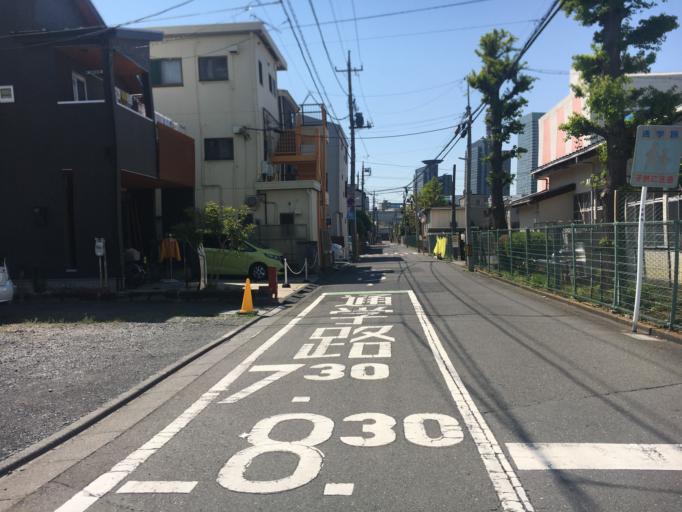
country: JP
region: Saitama
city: Yono
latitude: 35.9011
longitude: 139.6345
